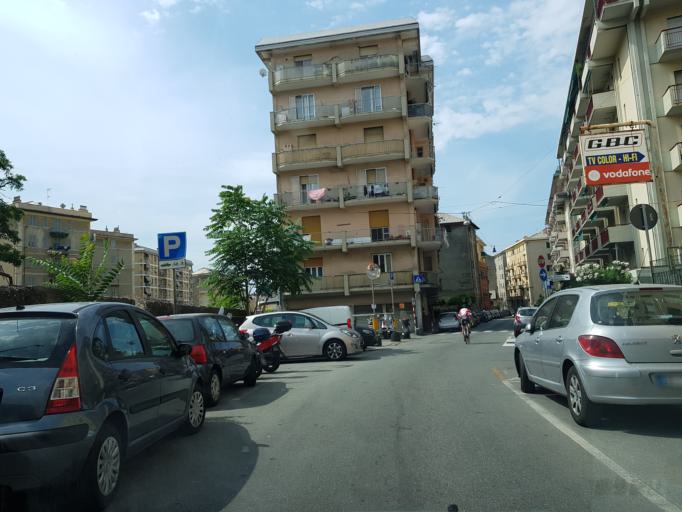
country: IT
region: Liguria
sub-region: Provincia di Genova
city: San Teodoro
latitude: 44.4278
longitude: 8.8540
